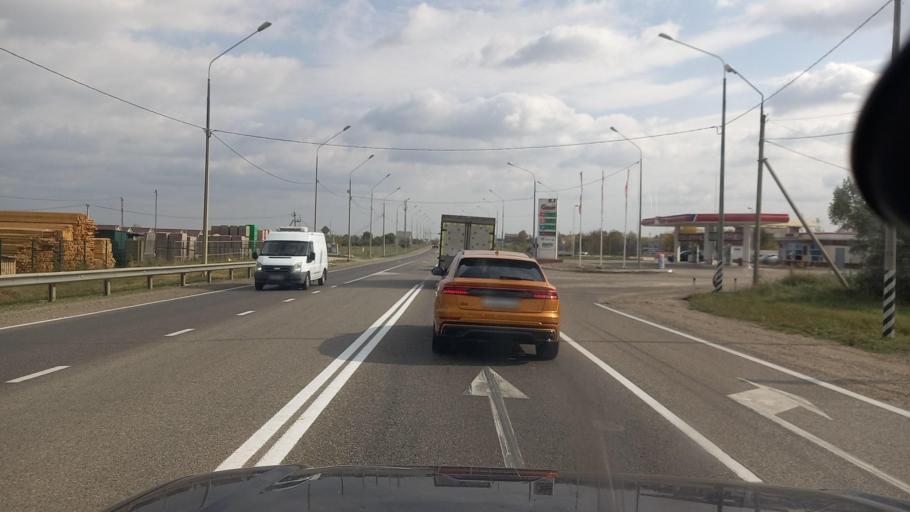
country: RU
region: Krasnodarskiy
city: Il'skiy
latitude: 44.8462
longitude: 38.5488
